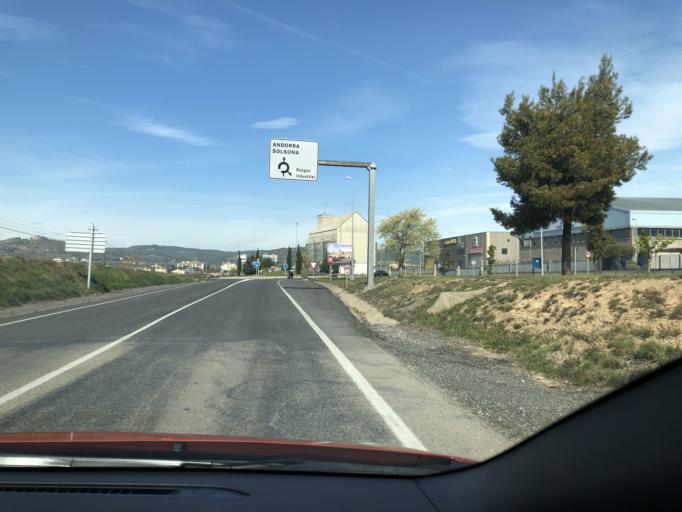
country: ES
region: Catalonia
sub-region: Provincia de Lleida
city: Solsona
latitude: 41.9909
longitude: 1.5406
